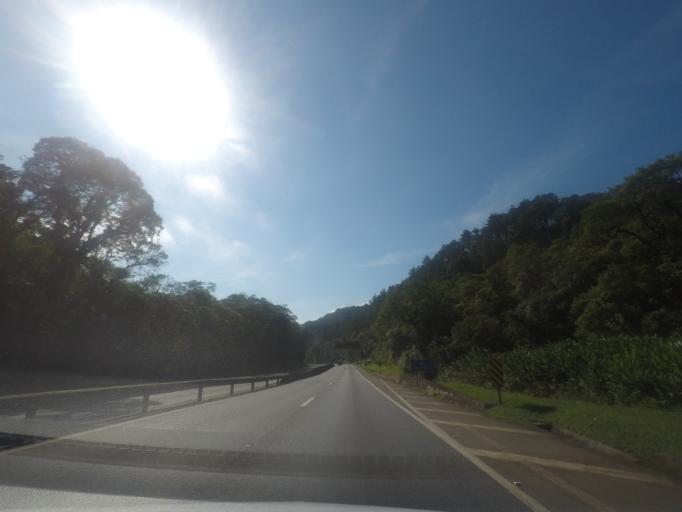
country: BR
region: Parana
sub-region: Piraquara
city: Piraquara
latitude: -25.5968
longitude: -48.9015
